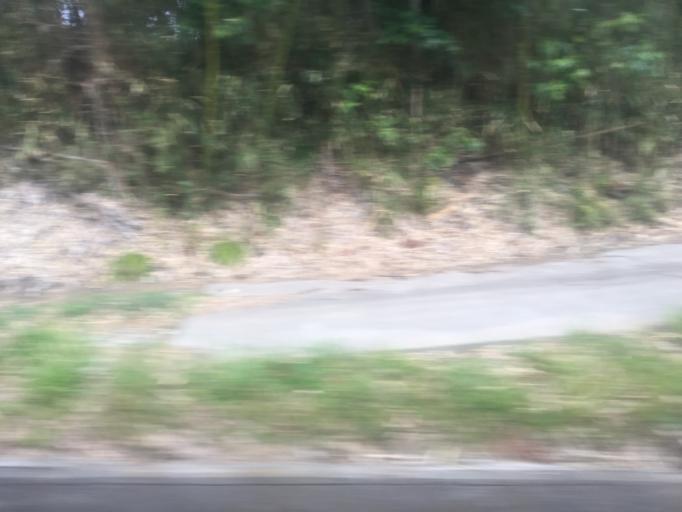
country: JP
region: Chiba
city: Yachimata
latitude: 35.6495
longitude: 140.3378
